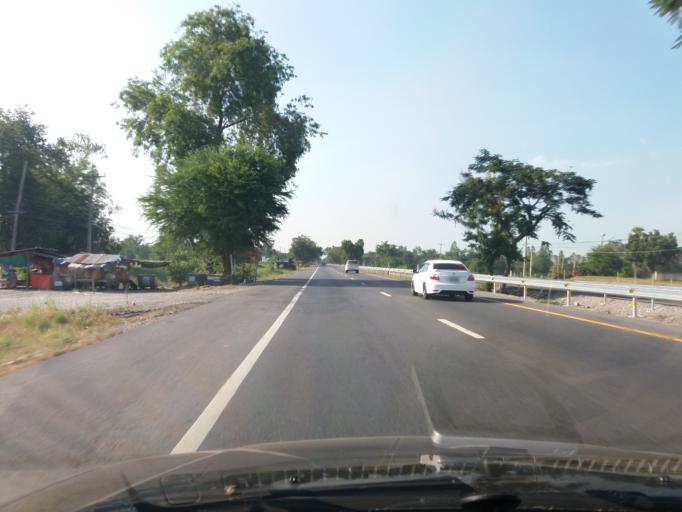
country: TH
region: Nakhon Sawan
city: Kao Liao
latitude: 15.7914
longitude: 99.9653
